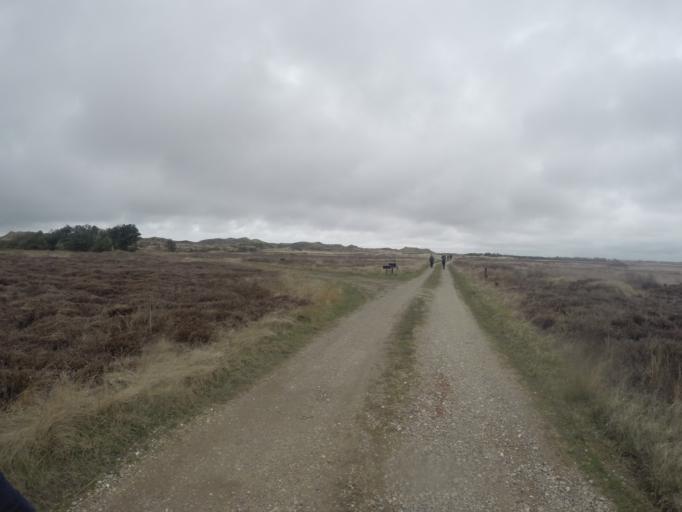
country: DK
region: North Denmark
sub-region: Thisted Kommune
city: Hurup
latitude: 56.8873
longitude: 8.3220
